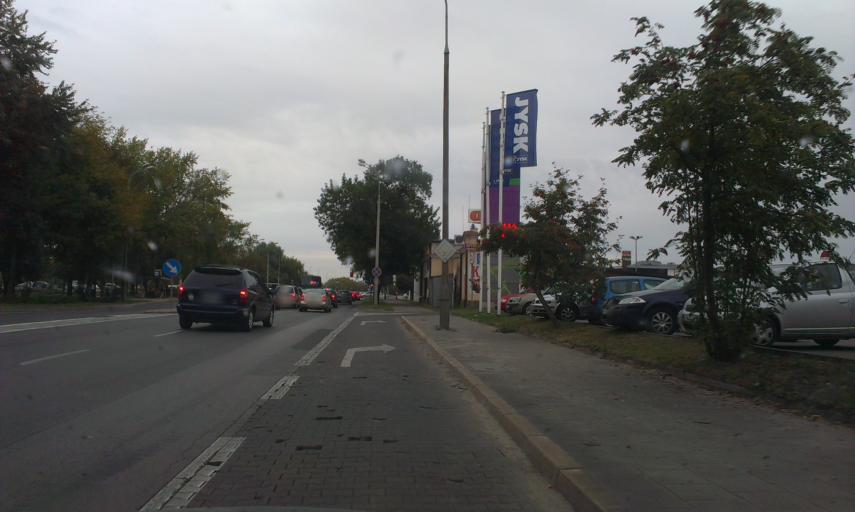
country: PL
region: Masovian Voivodeship
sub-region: Radom
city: Radom
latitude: 51.4074
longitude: 21.1420
